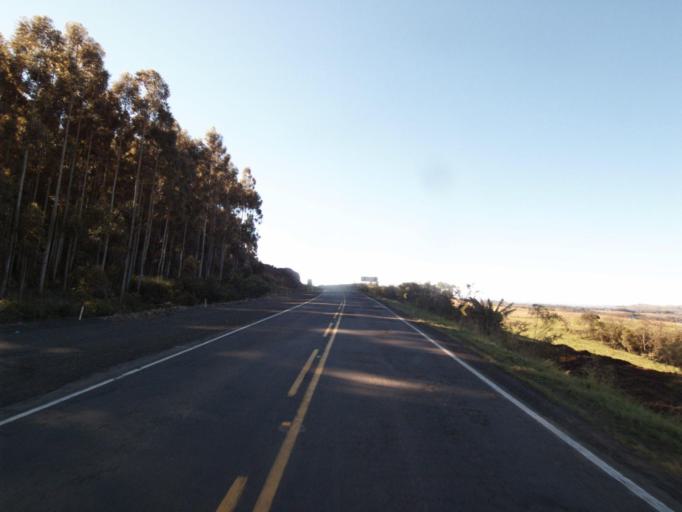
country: AR
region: Misiones
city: Bernardo de Irigoyen
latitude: -26.6283
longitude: -53.5165
